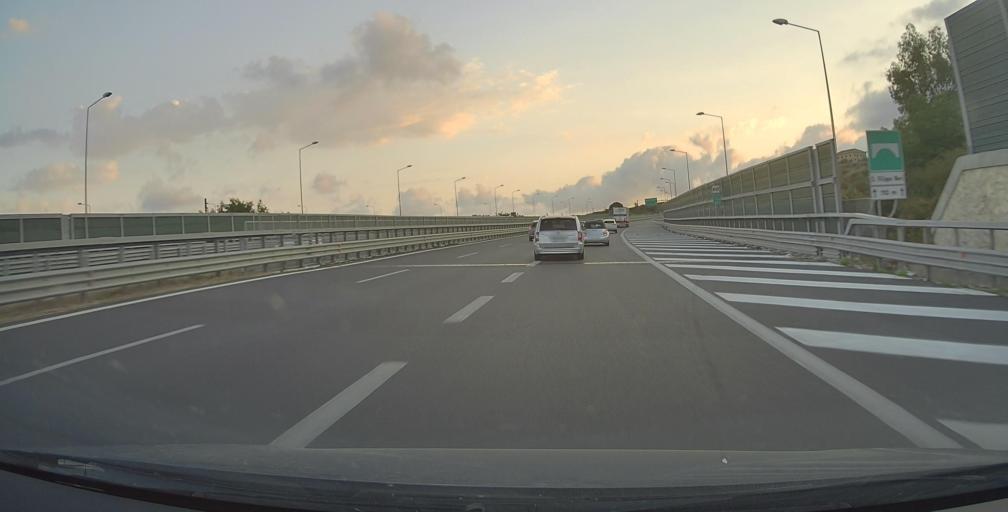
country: IT
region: Calabria
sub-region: Provincia di Reggio Calabria
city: Campo Calabro
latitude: 38.2079
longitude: 15.6422
